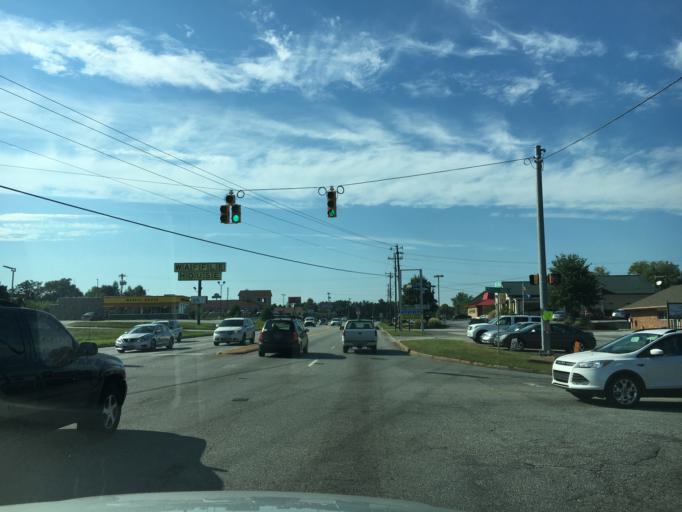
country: US
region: South Carolina
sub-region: Spartanburg County
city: Valley Falls
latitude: 35.0166
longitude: -81.9608
